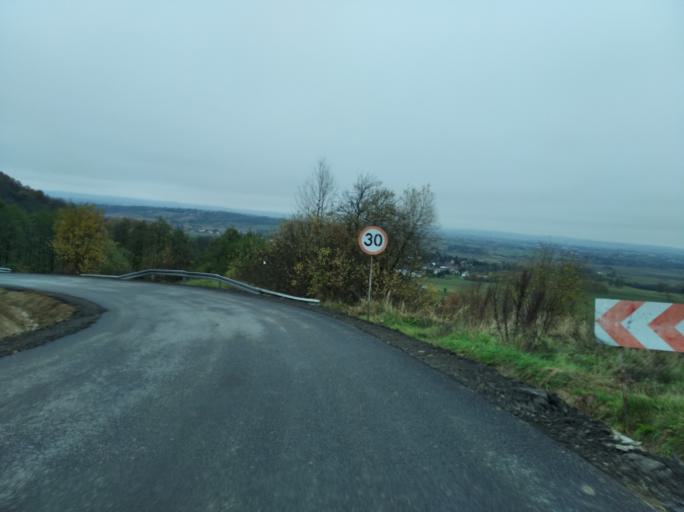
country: PL
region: Subcarpathian Voivodeship
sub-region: Powiat krosnienski
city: Odrzykon
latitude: 49.7386
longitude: 21.7730
